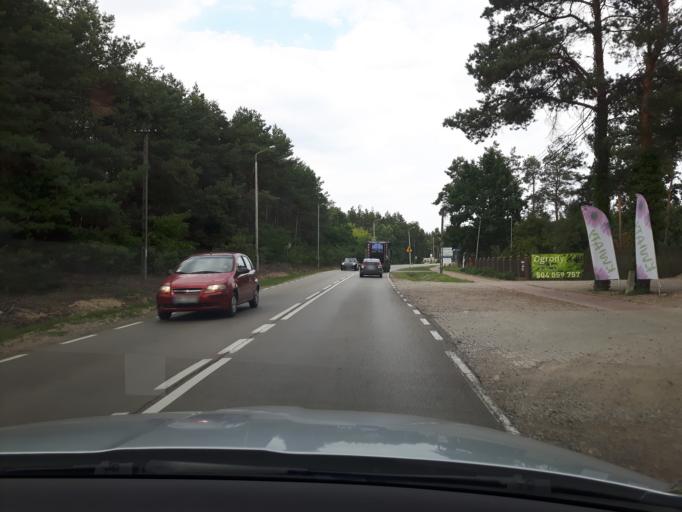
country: PL
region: Masovian Voivodeship
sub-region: Powiat legionowski
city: Stanislawow Pierwszy
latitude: 52.3822
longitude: 21.0292
